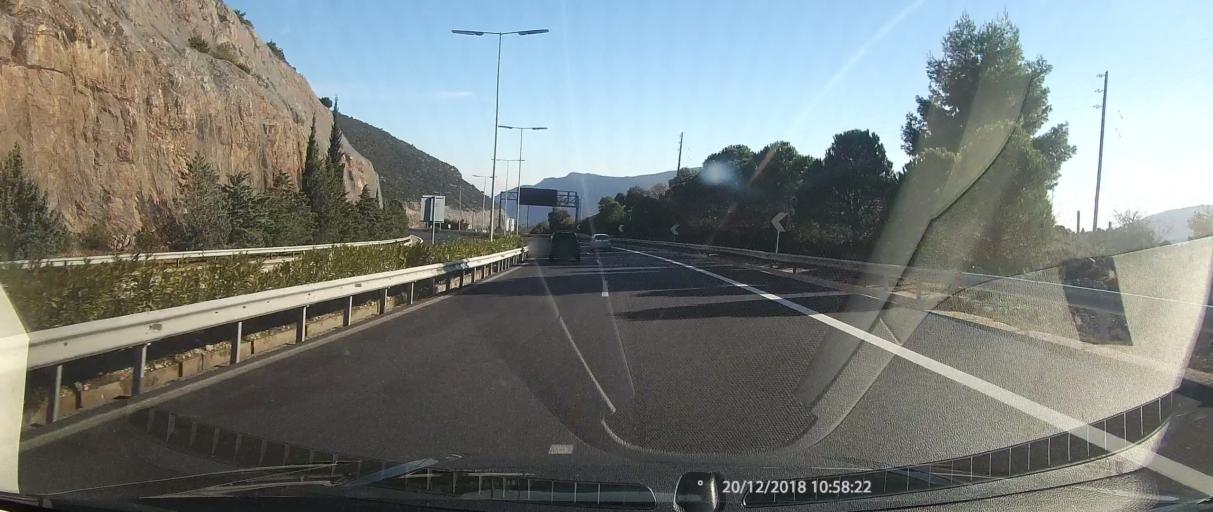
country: GR
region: Peloponnese
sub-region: Nomos Korinthias
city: Nemea
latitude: 37.6855
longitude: 22.5111
